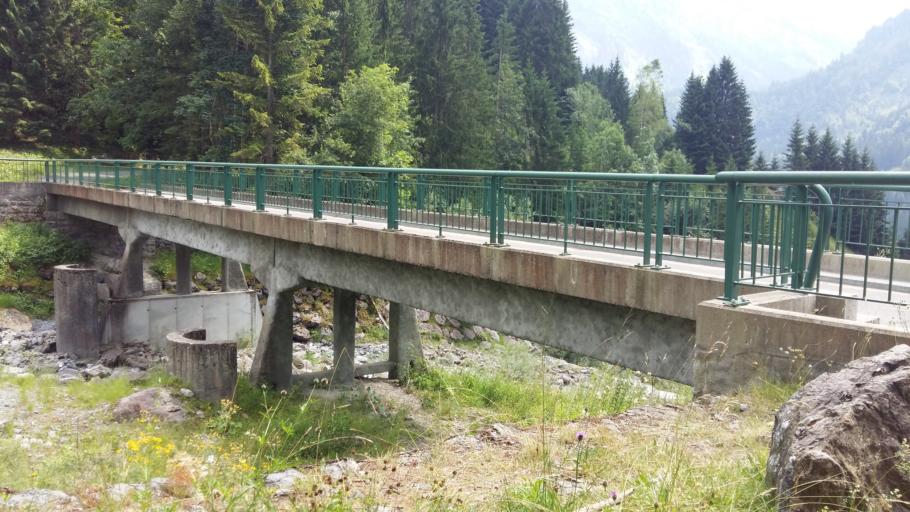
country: FR
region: Rhone-Alpes
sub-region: Departement de la Haute-Savoie
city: Samoens
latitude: 46.0412
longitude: 6.7745
